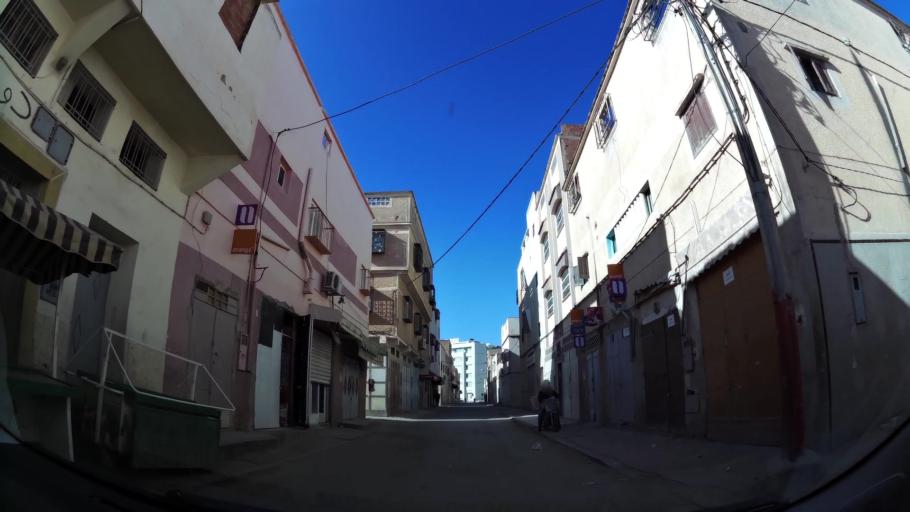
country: MA
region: Oriental
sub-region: Oujda-Angad
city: Oujda
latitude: 34.6803
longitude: -1.9278
